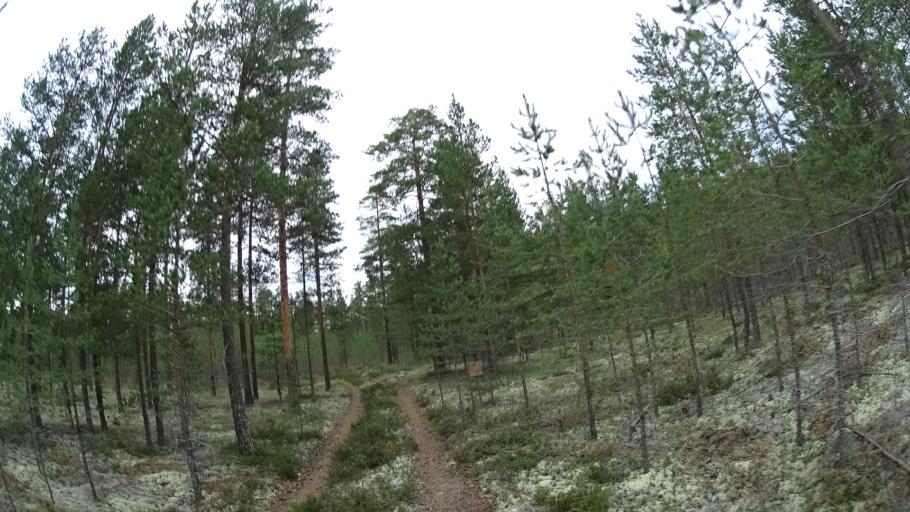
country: FI
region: Satakunta
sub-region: Pohjois-Satakunta
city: Jaemijaervi
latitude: 61.7642
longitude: 22.7609
